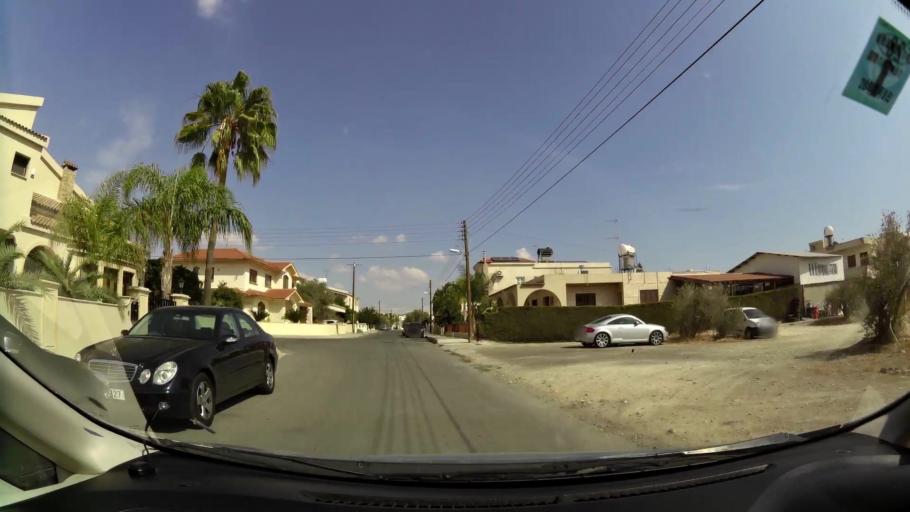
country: CY
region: Larnaka
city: Aradippou
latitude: 34.9394
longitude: 33.5897
